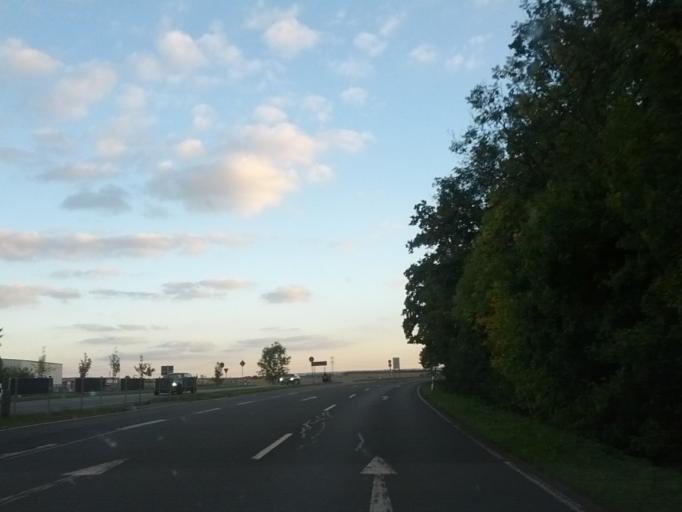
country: DE
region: Thuringia
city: Rockhausen
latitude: 50.9375
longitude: 11.0400
